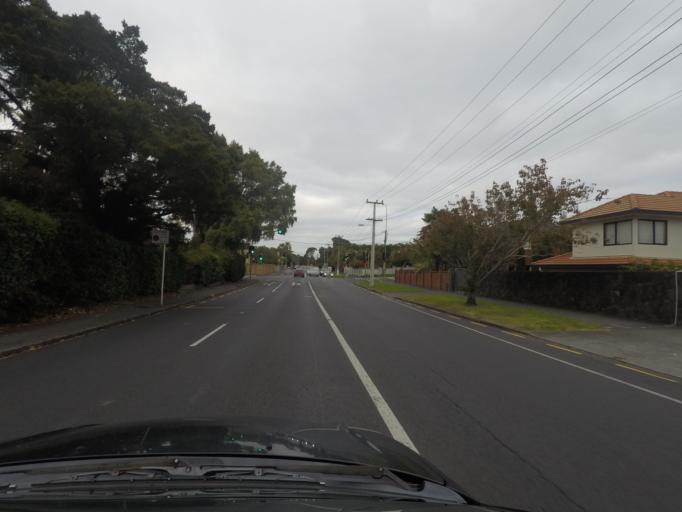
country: NZ
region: Auckland
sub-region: Auckland
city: Auckland
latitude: -36.8823
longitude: 174.7717
